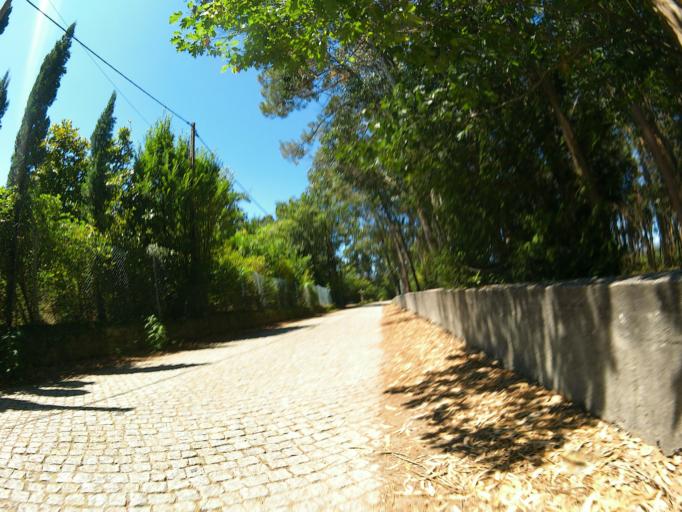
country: PT
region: Viana do Castelo
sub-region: Viana do Castelo
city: Darque
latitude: 41.6866
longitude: -8.7698
